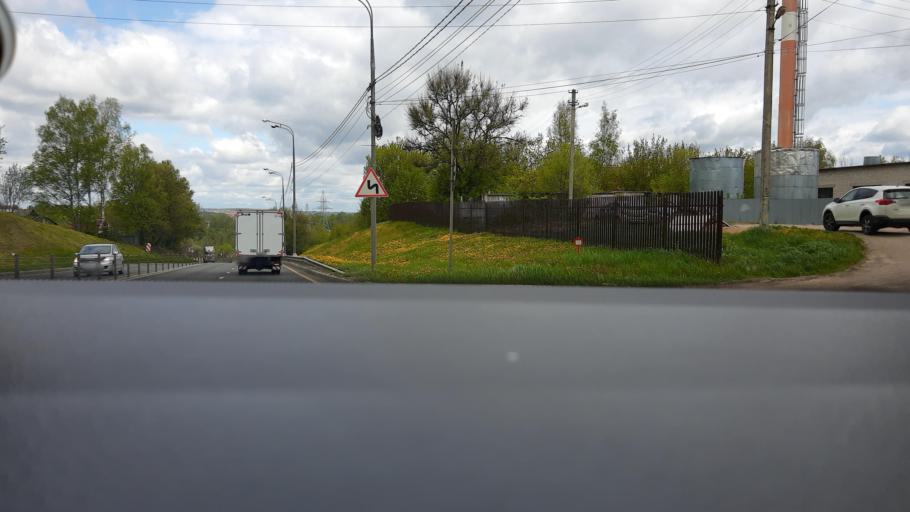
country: RU
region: Moskovskaya
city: Dedenevo
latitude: 56.2467
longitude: 37.5213
